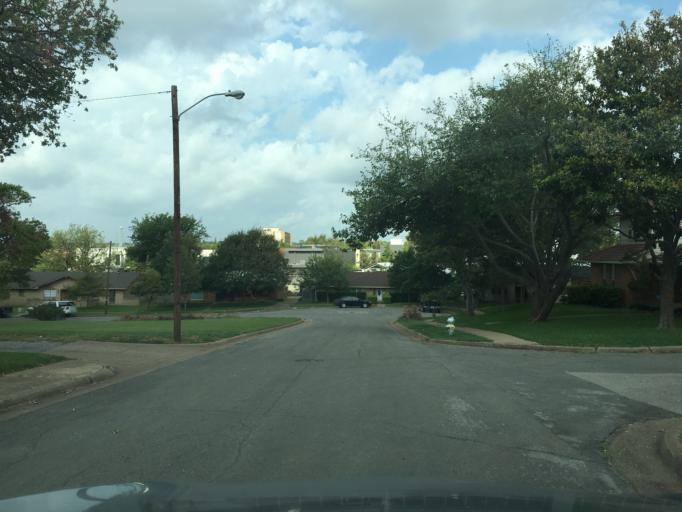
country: US
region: Texas
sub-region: Dallas County
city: Richardson
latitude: 32.9021
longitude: -96.7622
